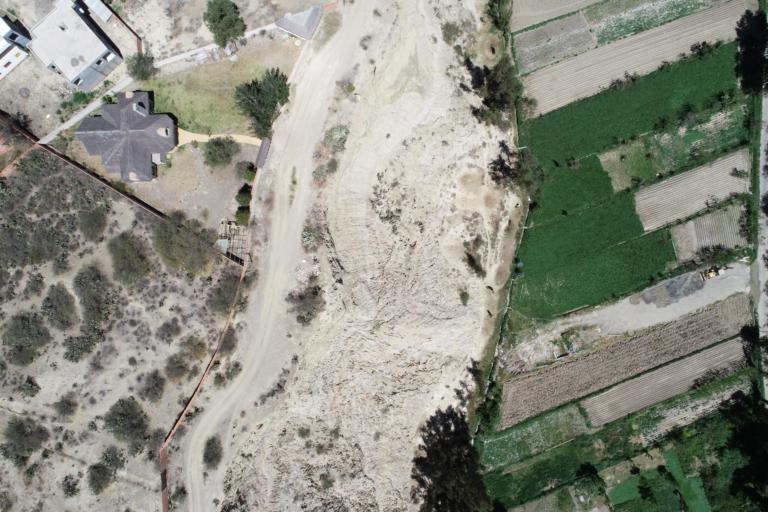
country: BO
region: La Paz
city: La Paz
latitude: -16.6489
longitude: -68.0449
